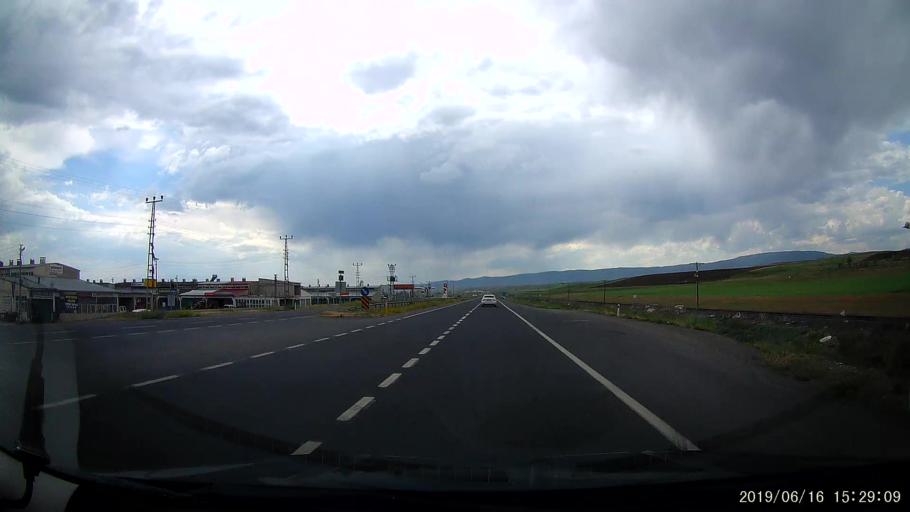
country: TR
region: Erzurum
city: Horasan
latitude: 40.0314
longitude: 42.1387
